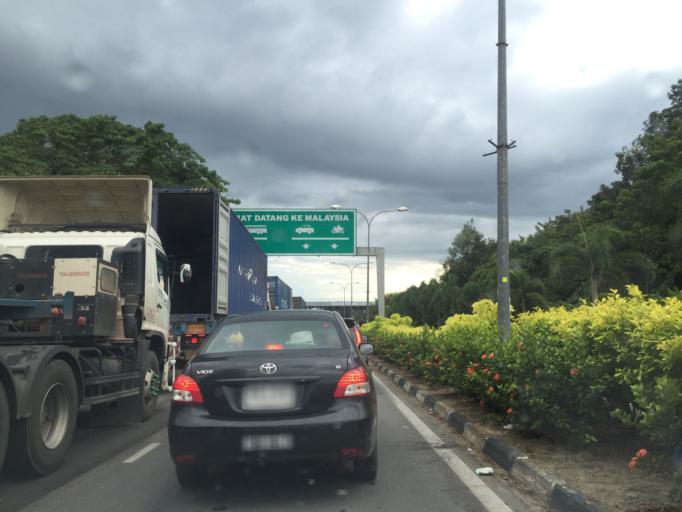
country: TH
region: Songkhla
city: Sadao
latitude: 6.5153
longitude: 100.4197
